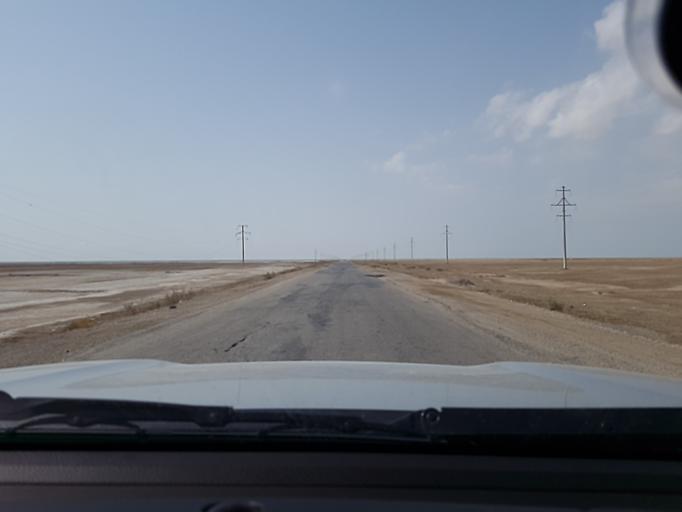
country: TM
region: Balkan
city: Gumdag
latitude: 39.0941
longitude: 54.5840
